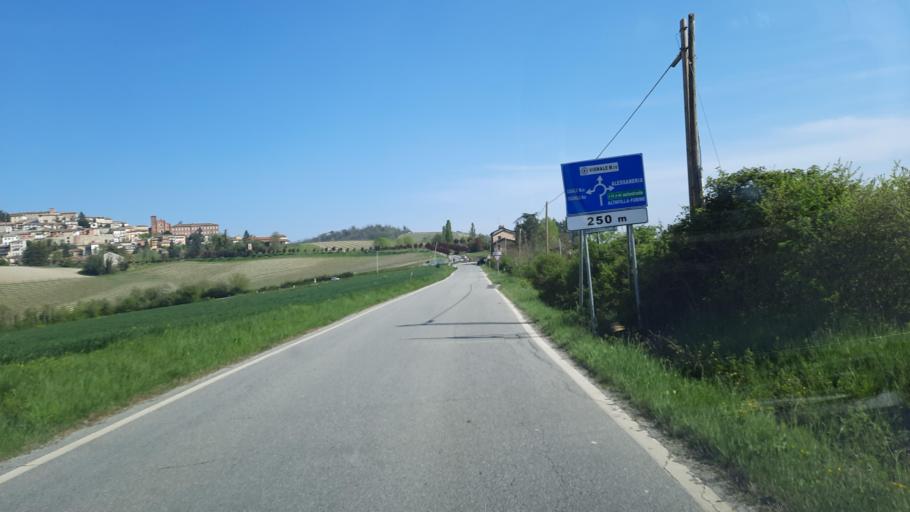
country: IT
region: Piedmont
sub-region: Provincia di Alessandria
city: Vignale Monferrato
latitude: 45.0114
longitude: 8.3841
